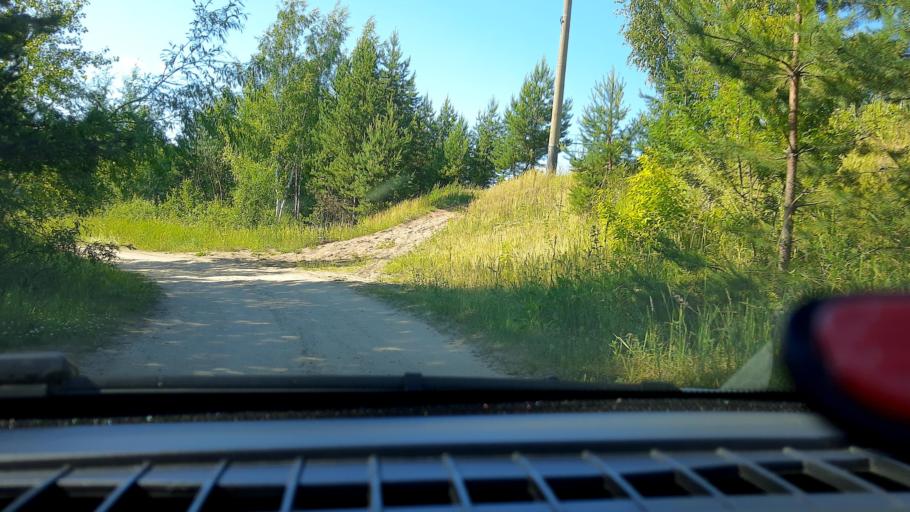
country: RU
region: Nizjnij Novgorod
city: Gidrotorf
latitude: 56.5061
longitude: 43.5384
